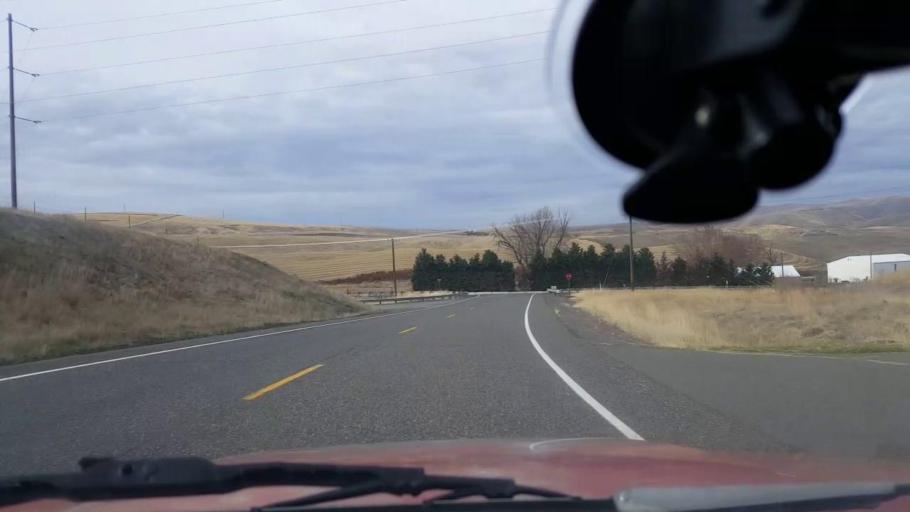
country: US
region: Washington
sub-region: Asotin County
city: Clarkston Heights-Vineland
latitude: 46.3993
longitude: -117.0996
